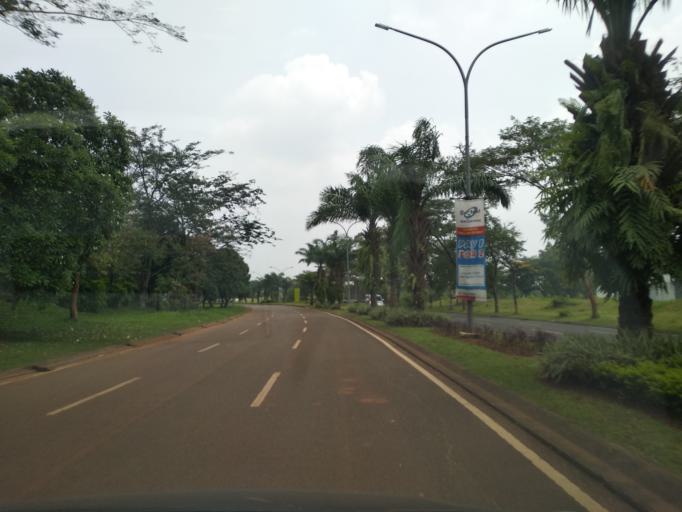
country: ID
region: West Java
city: Bekasi
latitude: -6.2946
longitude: 107.0486
